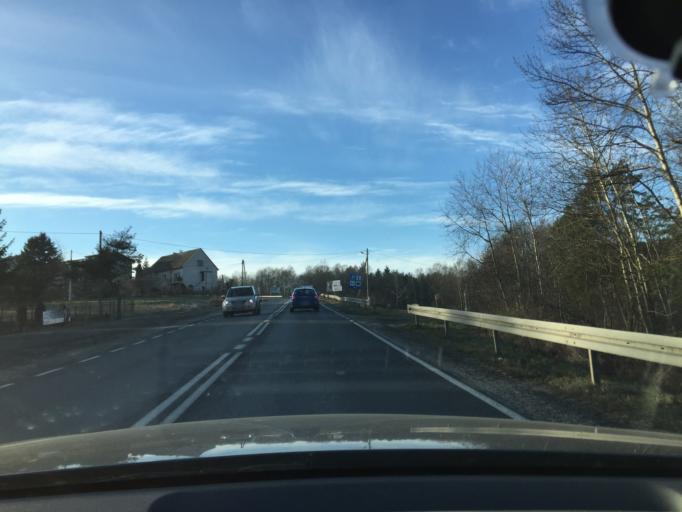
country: PL
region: Lesser Poland Voivodeship
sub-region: Powiat wadowicki
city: Izdebnik
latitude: 49.8652
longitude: 19.7471
